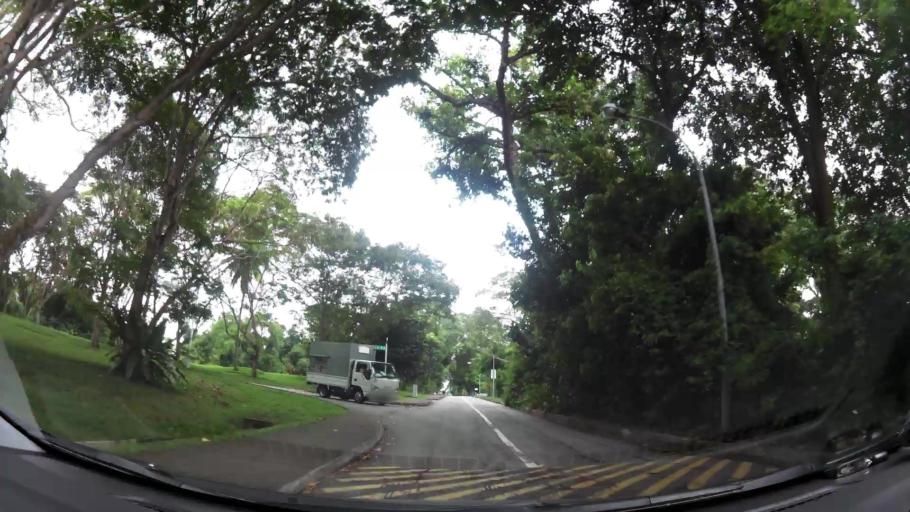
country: SG
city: Singapore
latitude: 1.2831
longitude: 103.7999
